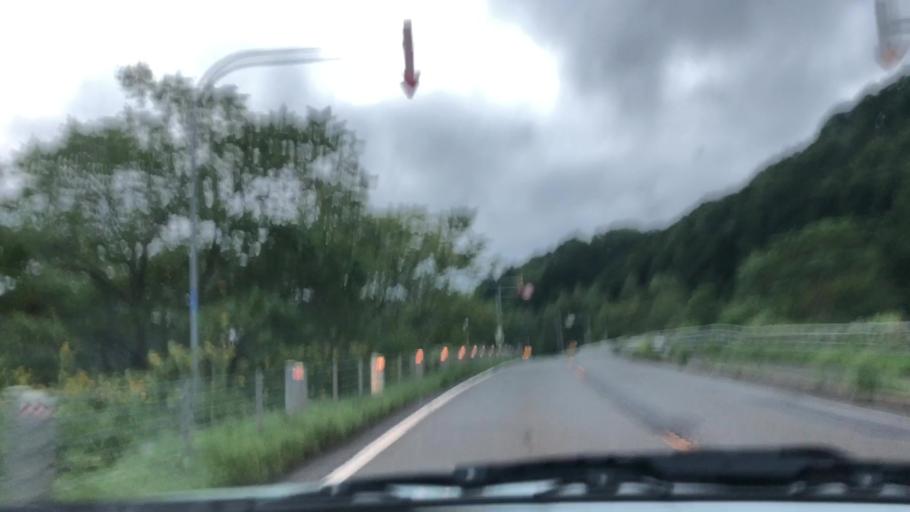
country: JP
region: Hokkaido
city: Chitose
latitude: 42.9070
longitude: 141.9894
